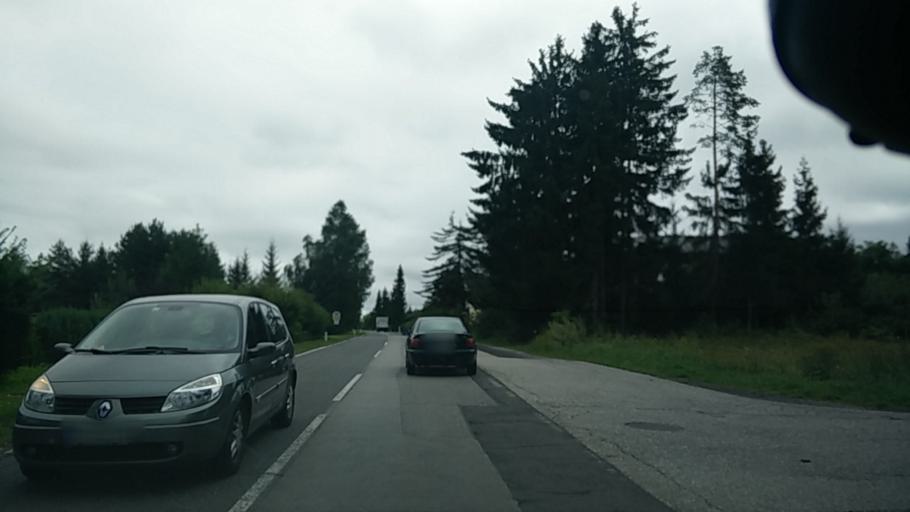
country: AT
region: Carinthia
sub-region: Politischer Bezirk Villach Land
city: Wernberg
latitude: 46.5564
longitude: 13.9600
